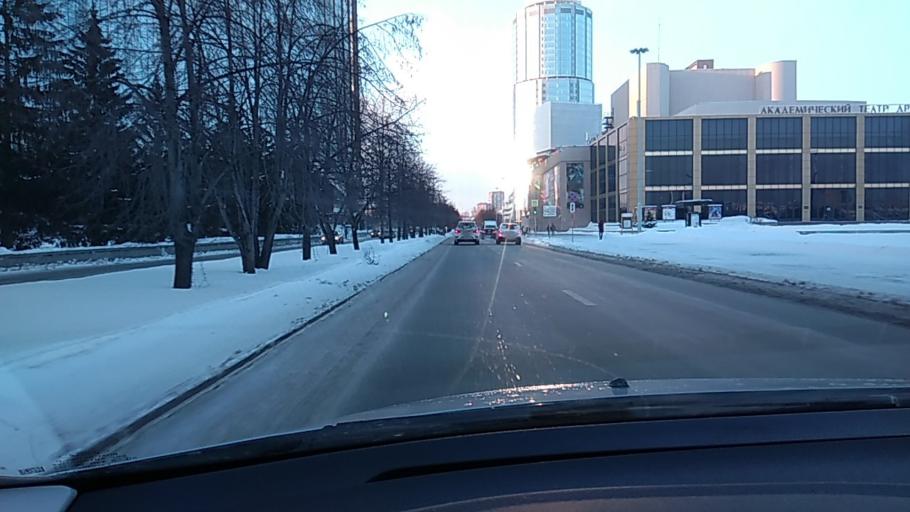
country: RU
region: Sverdlovsk
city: Yekaterinburg
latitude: 56.8425
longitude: 60.5948
